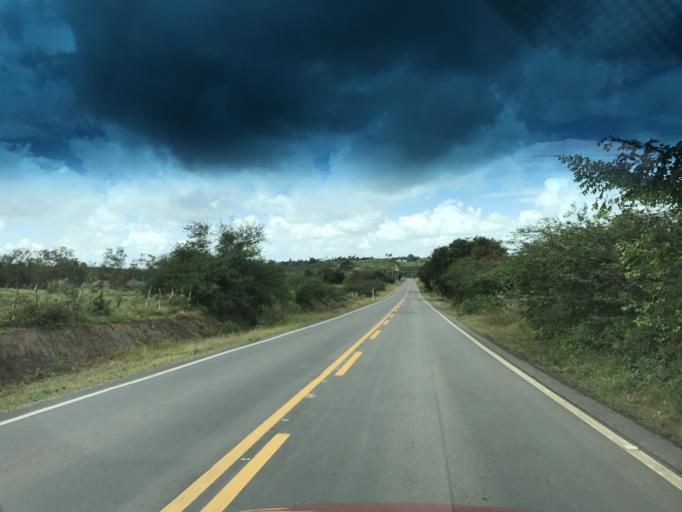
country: BR
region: Bahia
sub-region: Conceicao Do Almeida
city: Conceicao do Almeida
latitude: -12.7057
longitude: -39.2339
